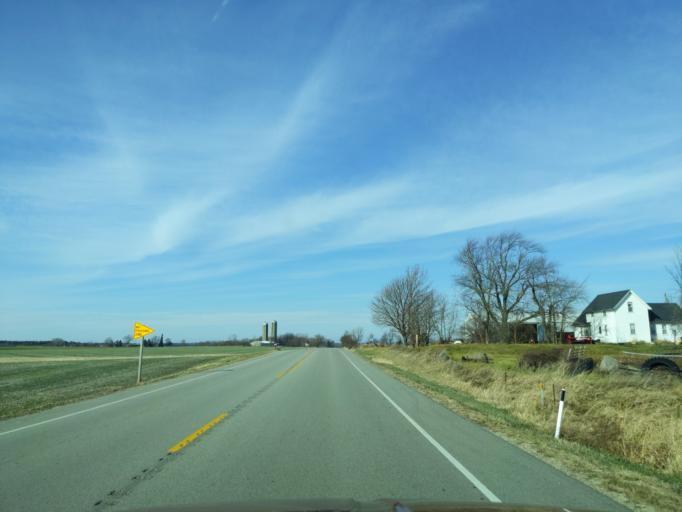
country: US
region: Wisconsin
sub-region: Walworth County
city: Elkhorn
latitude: 42.7000
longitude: -88.5715
